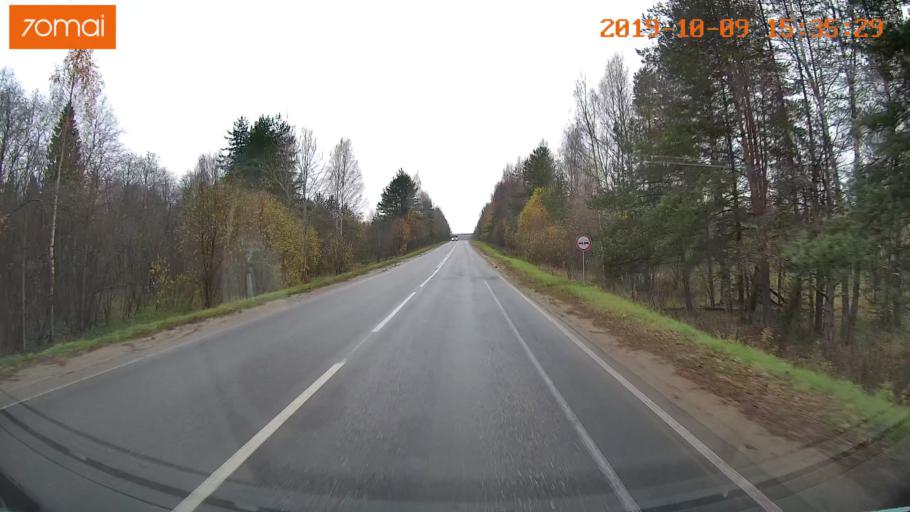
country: RU
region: Kostroma
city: Oktyabr'skiy
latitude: 57.9316
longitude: 41.2263
